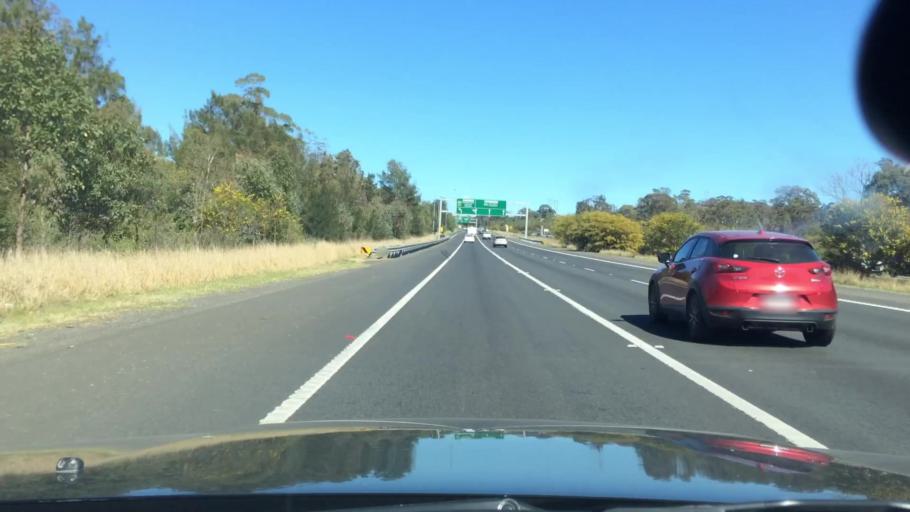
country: AU
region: New South Wales
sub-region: Campbelltown Municipality
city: Campbelltown
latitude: -34.0561
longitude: 150.7993
